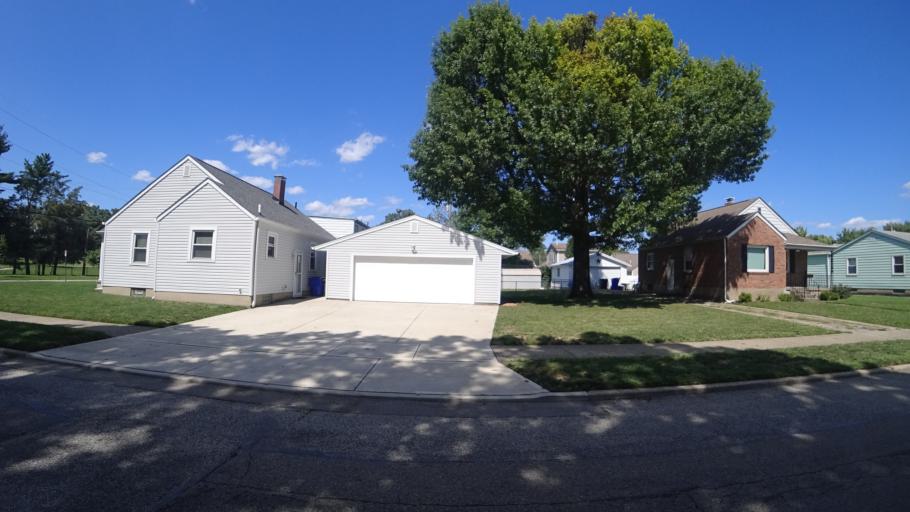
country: US
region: Ohio
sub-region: Butler County
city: Hamilton
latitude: 39.4056
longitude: -84.5372
